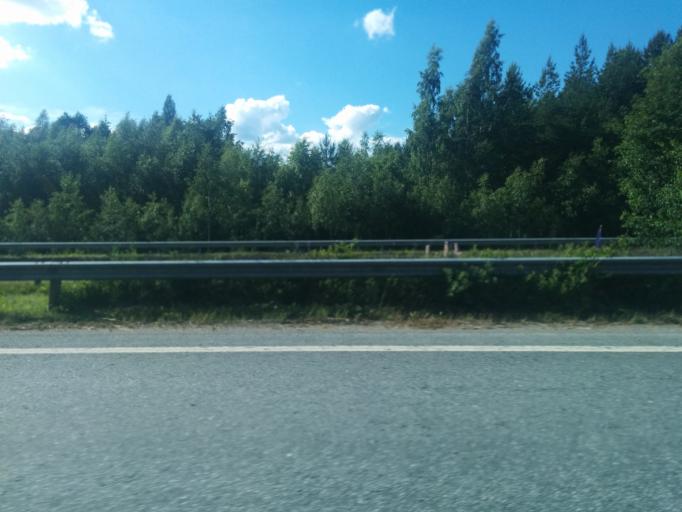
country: FI
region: Pirkanmaa
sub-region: Tampere
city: Tampere
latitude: 61.5036
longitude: 23.8962
